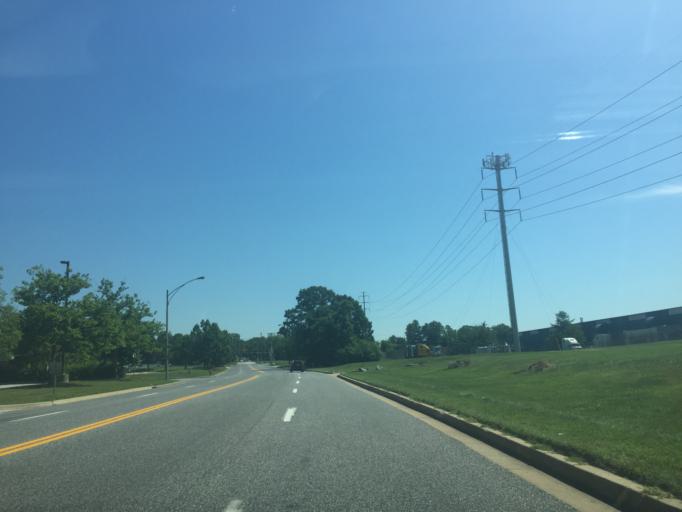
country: US
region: Maryland
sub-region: Baltimore County
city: Rossville
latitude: 39.3389
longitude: -76.4670
